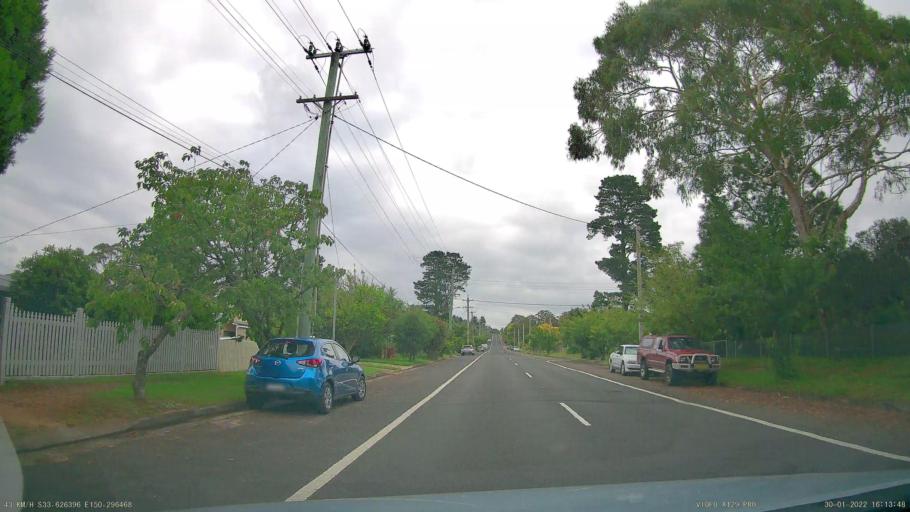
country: AU
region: New South Wales
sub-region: Blue Mountains Municipality
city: Blackheath
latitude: -33.6265
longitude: 150.2964
